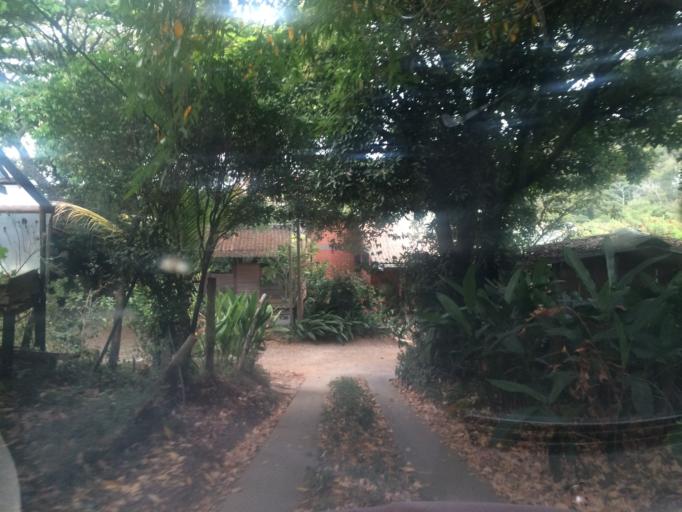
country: CO
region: Valle del Cauca
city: Cali
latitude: 3.4396
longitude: -76.5577
